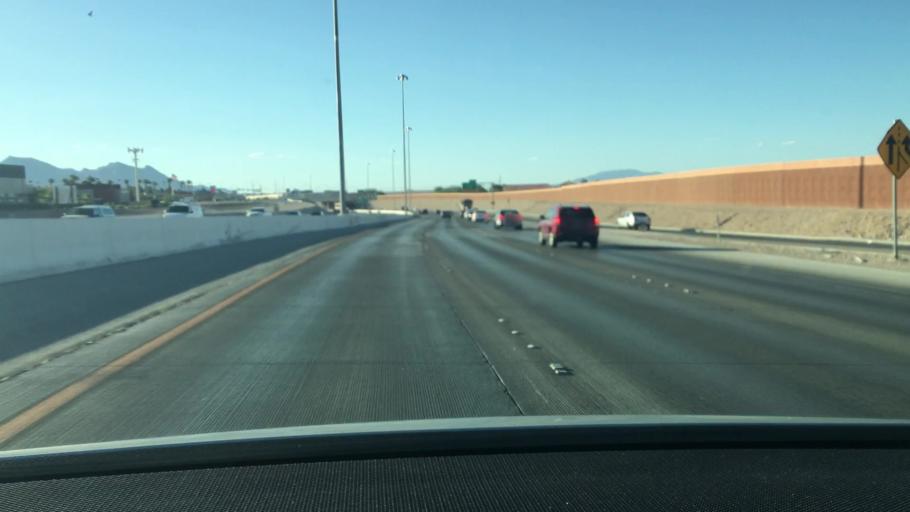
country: US
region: Nevada
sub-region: Clark County
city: Summerlin South
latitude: 36.1027
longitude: -115.2950
